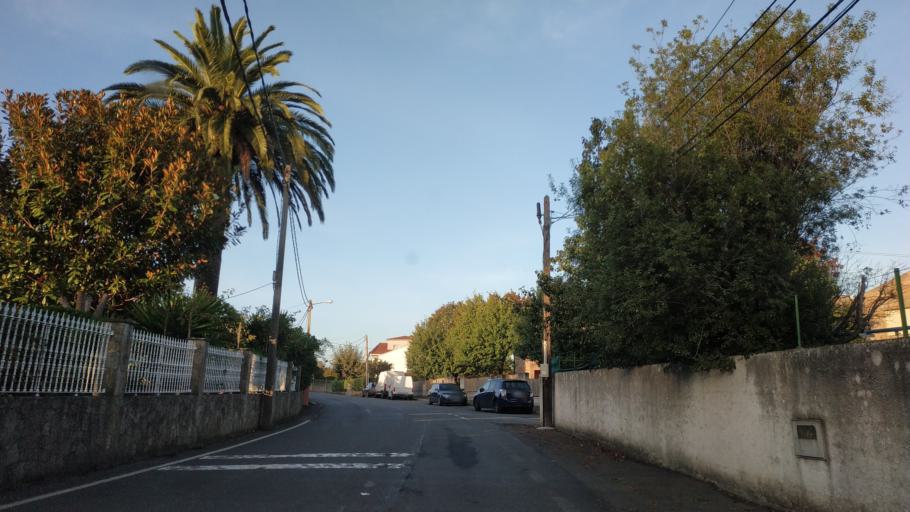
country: ES
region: Galicia
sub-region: Provincia da Coruna
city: Oleiros
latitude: 43.3541
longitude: -8.3443
